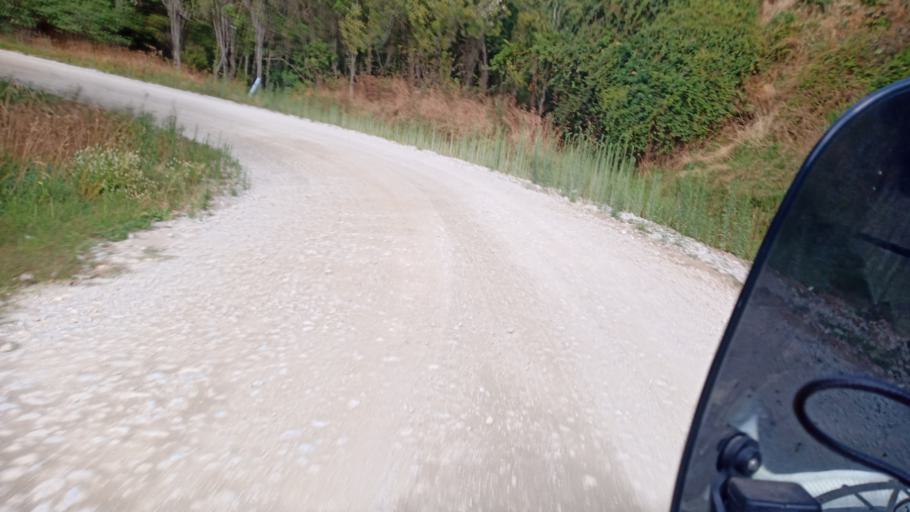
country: NZ
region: Hawke's Bay
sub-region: Wairoa District
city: Wairoa
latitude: -38.6058
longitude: 177.4645
